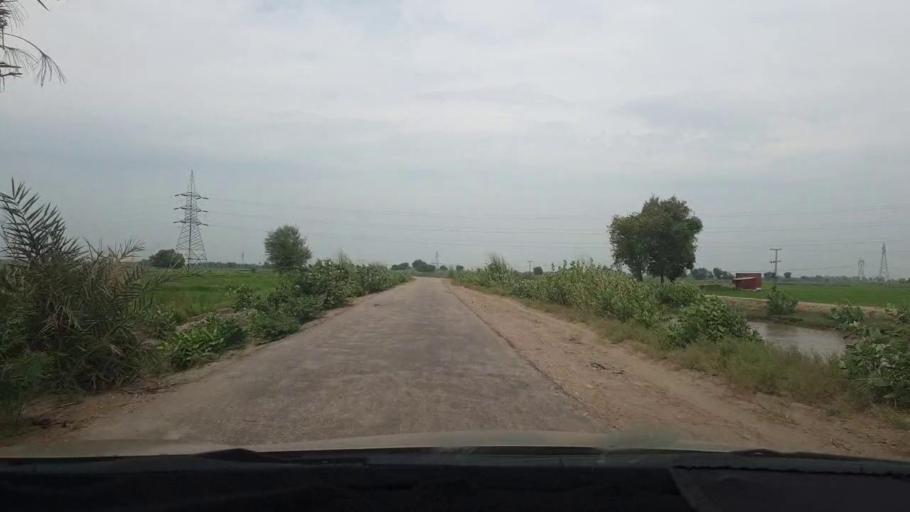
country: PK
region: Sindh
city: Naudero
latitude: 27.6792
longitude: 68.3521
